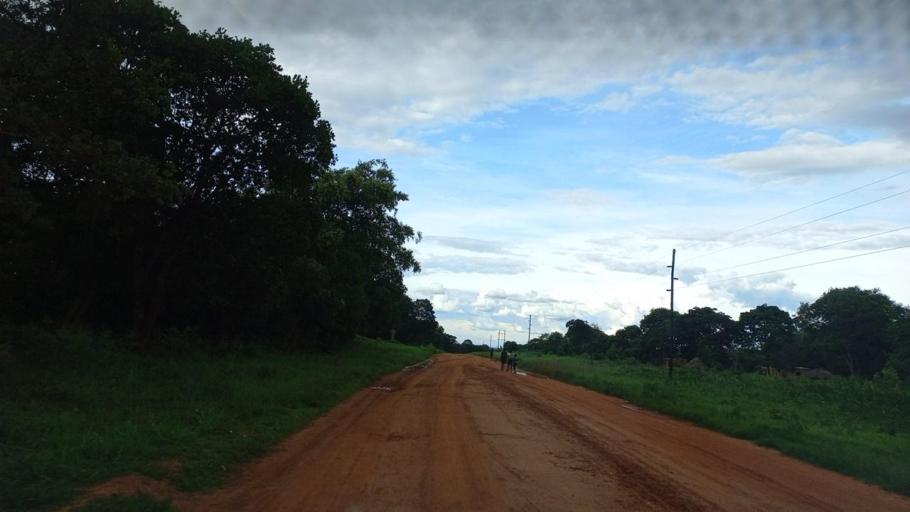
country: ZM
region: North-Western
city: Mwinilunga
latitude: -11.7714
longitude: 24.4073
